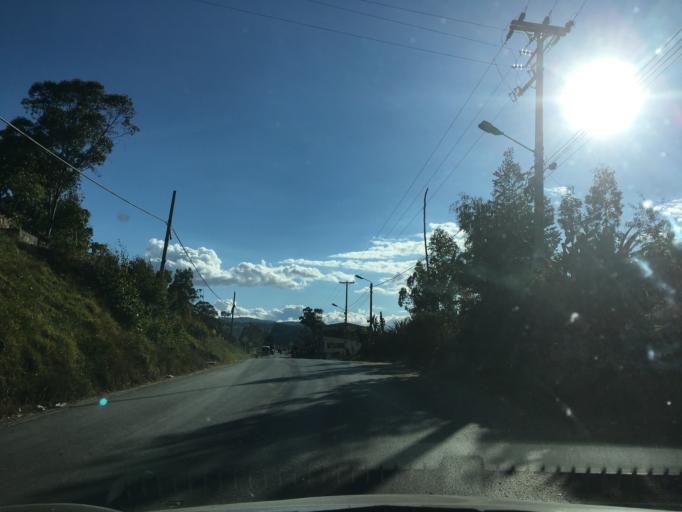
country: CO
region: Boyaca
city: Firavitoba
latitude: 5.6780
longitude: -72.9581
